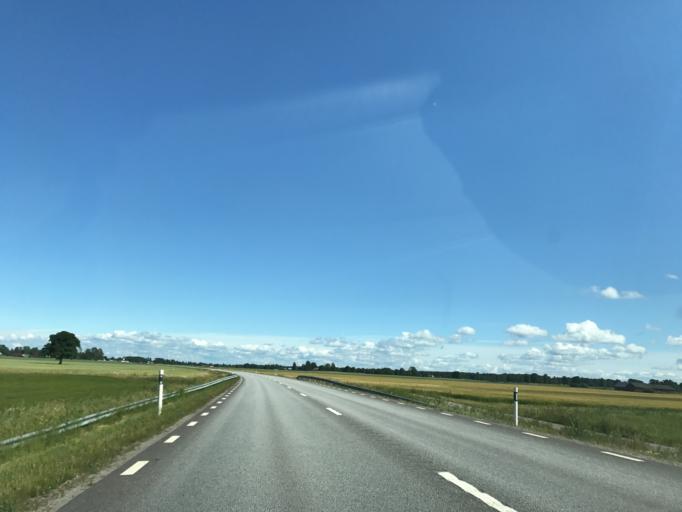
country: SE
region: OErebro
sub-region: Orebro Kommun
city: Odensbacken
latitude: 59.1532
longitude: 15.4907
